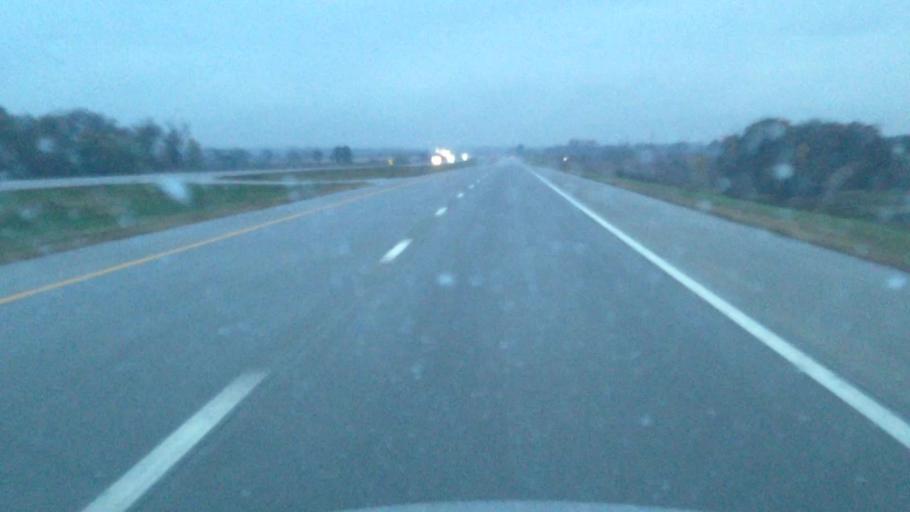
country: US
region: Kansas
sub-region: Douglas County
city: Baldwin City
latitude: 38.7369
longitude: -95.2679
